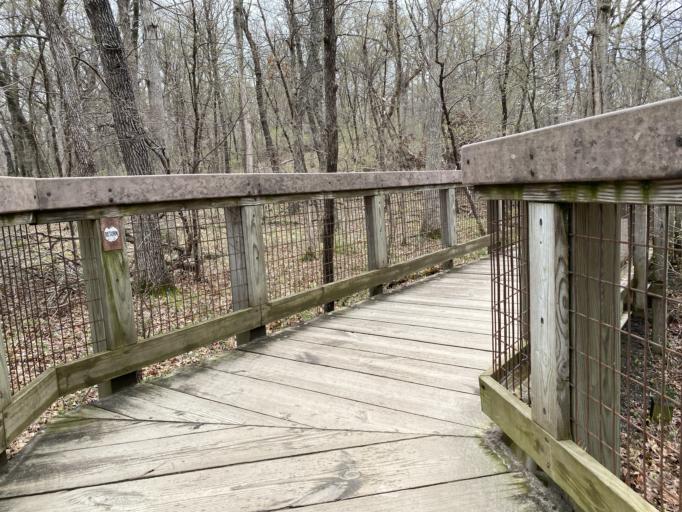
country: US
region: Illinois
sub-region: LaSalle County
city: Deer Park
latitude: 41.3163
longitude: -88.9828
